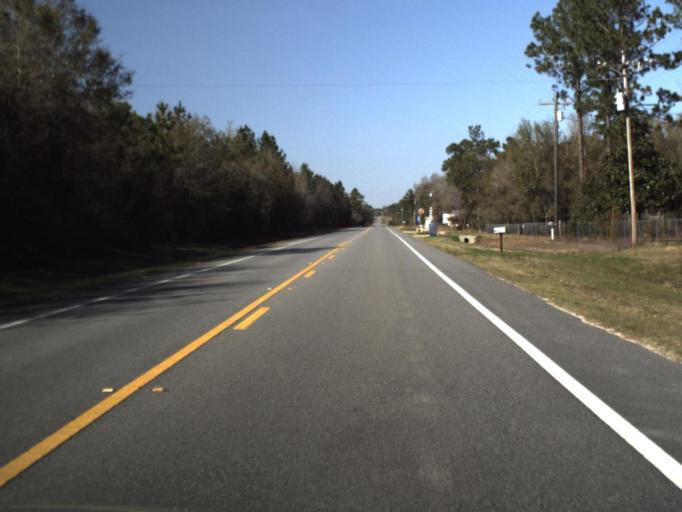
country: US
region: Florida
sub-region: Gulf County
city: Wewahitchka
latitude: 30.2685
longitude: -85.2421
